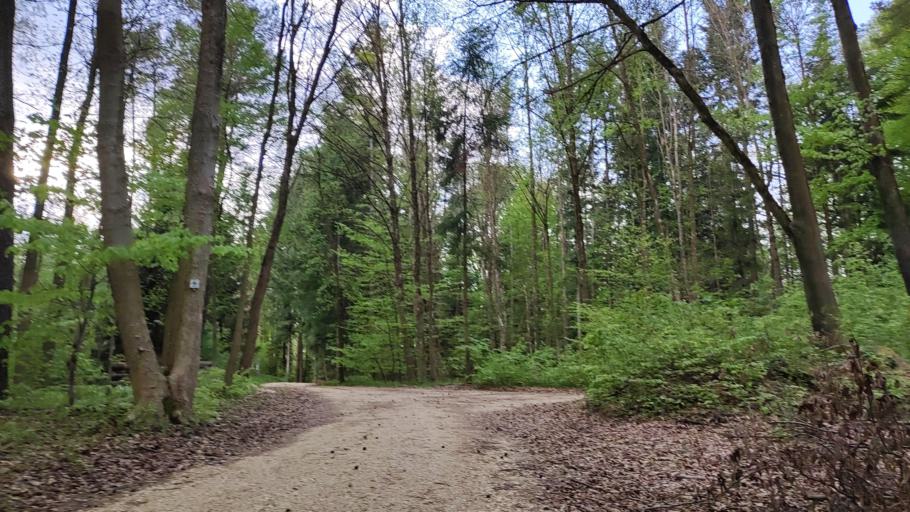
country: DE
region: Bavaria
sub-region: Swabia
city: Zusmarshausen
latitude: 48.3995
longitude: 10.6169
